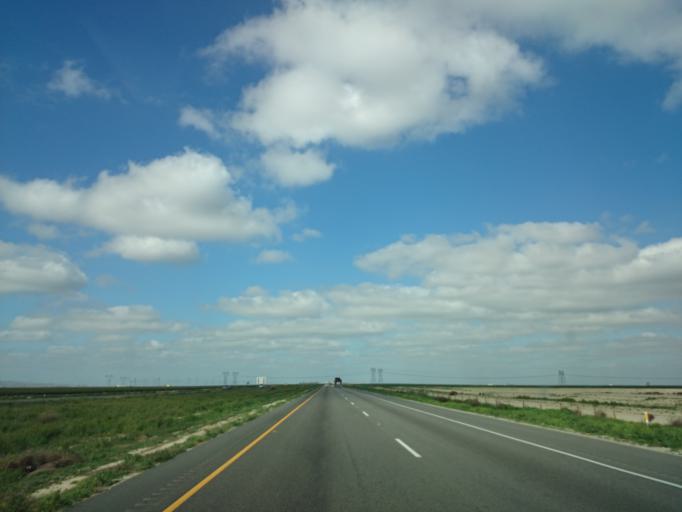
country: US
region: California
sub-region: Kern County
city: Rosedale
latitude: 35.2197
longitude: -119.1740
